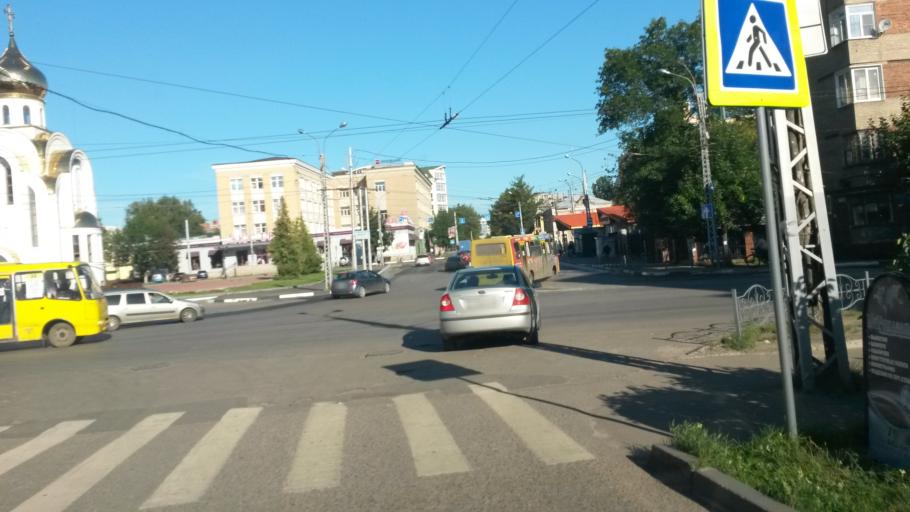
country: RU
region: Ivanovo
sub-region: Gorod Ivanovo
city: Ivanovo
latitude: 56.9929
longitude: 40.9763
